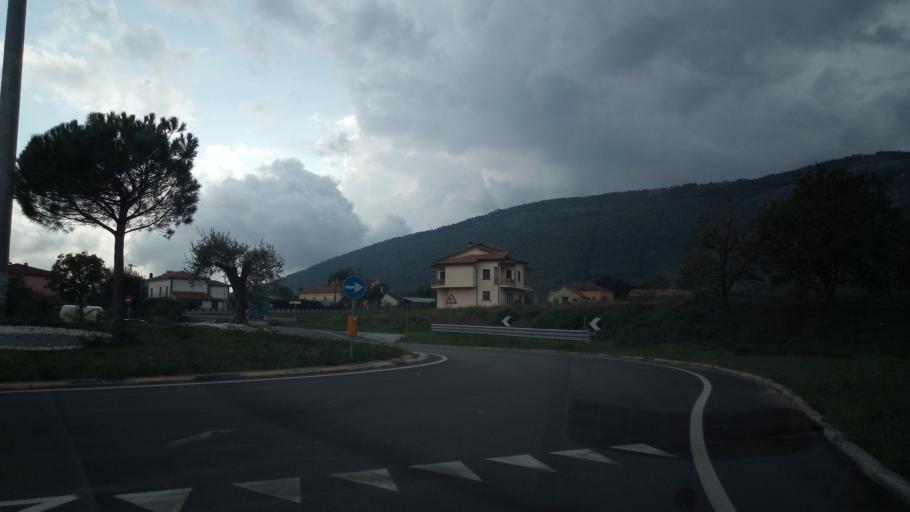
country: IT
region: Campania
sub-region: Provincia di Salerno
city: Buonabitacolo
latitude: 40.2857
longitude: 15.6363
